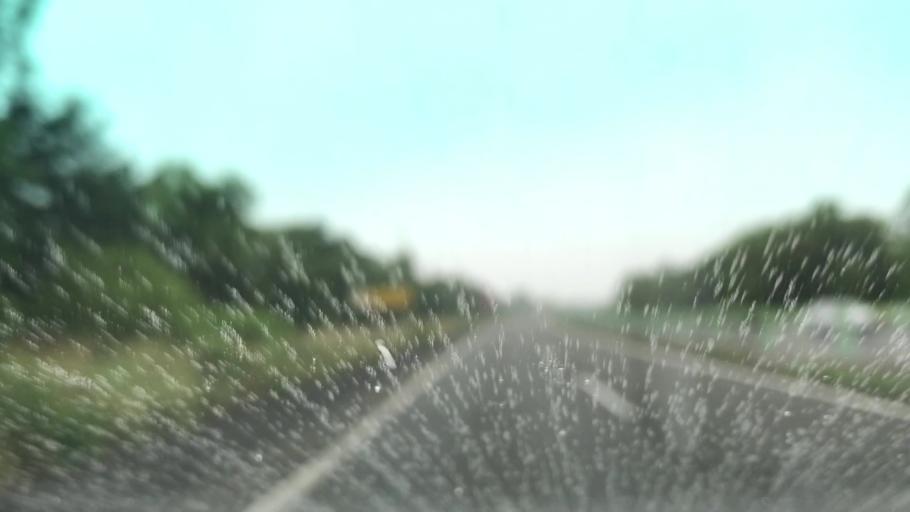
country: JP
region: Hokkaido
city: Shiraoi
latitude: 42.5141
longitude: 141.2699
